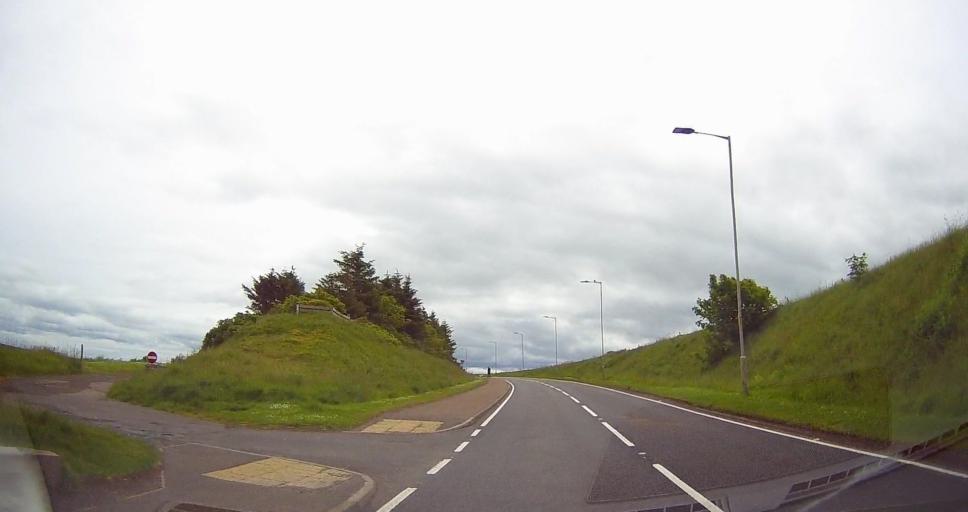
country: GB
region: Scotland
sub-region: Highland
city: Thurso
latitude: 58.6060
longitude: -3.5509
